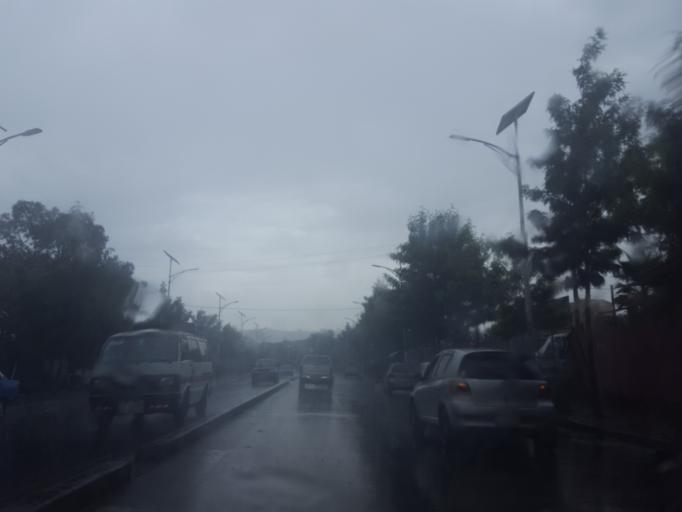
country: ET
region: Adis Abeba
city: Addis Ababa
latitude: 9.0199
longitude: 38.7824
